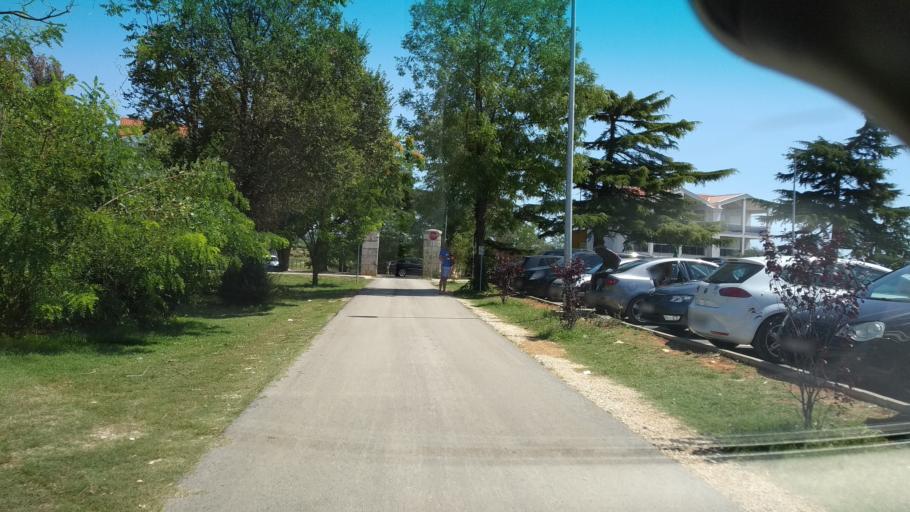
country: HR
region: Istarska
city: Fazana
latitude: 44.9217
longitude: 13.8068
